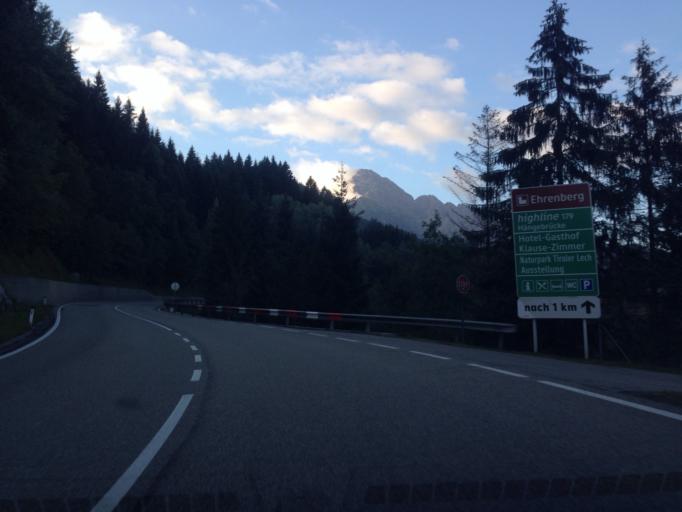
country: AT
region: Tyrol
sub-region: Politischer Bezirk Reutte
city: Breitenwang
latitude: 47.4760
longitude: 10.7281
